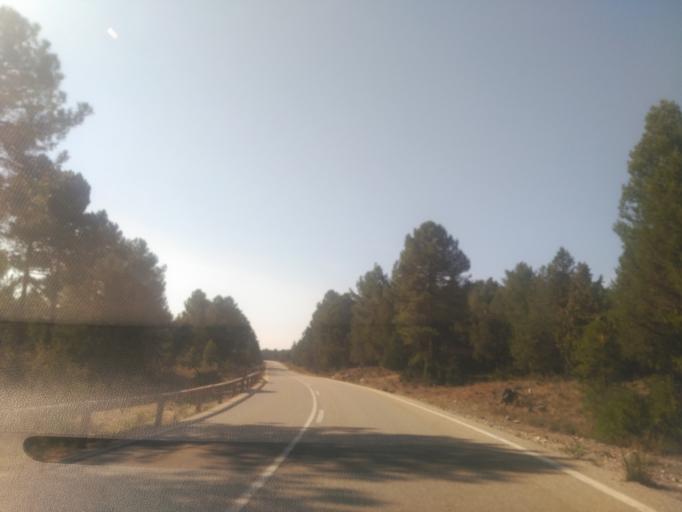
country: ES
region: Castille and Leon
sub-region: Provincia de Soria
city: Ucero
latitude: 41.7433
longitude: -3.0449
